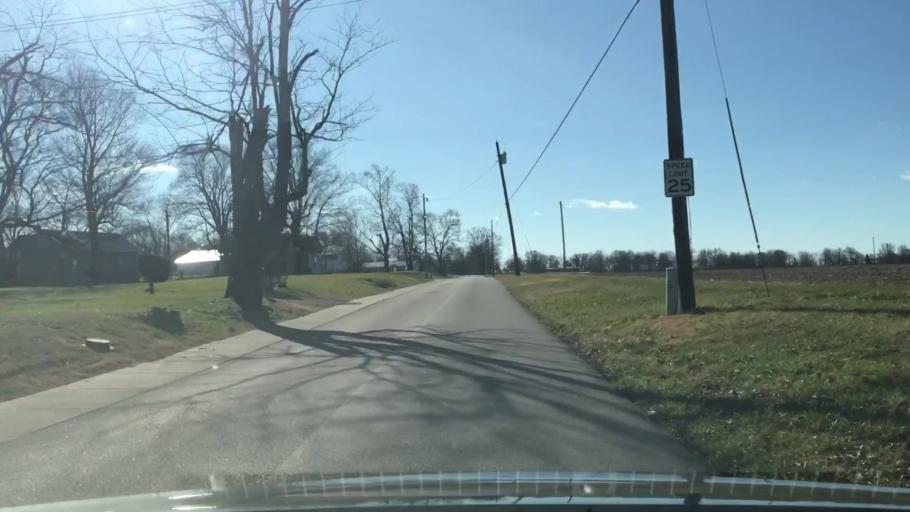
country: US
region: Kentucky
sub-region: Edmonson County
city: Brownsville
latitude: 37.0573
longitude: -86.2111
